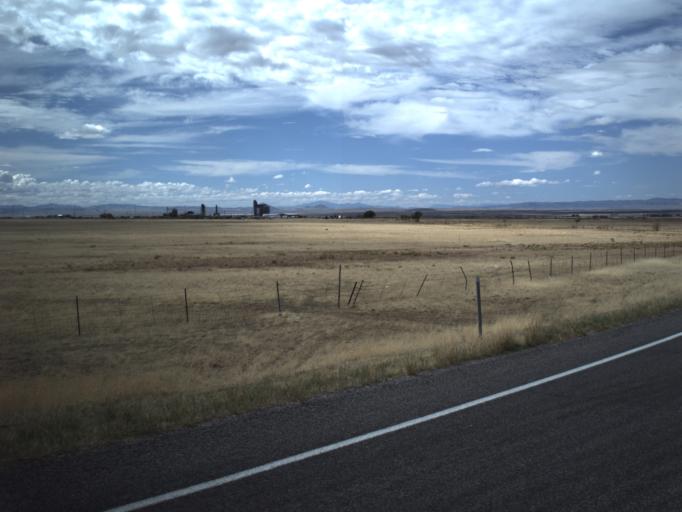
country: US
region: Utah
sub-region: Millard County
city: Fillmore
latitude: 38.9792
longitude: -112.3411
